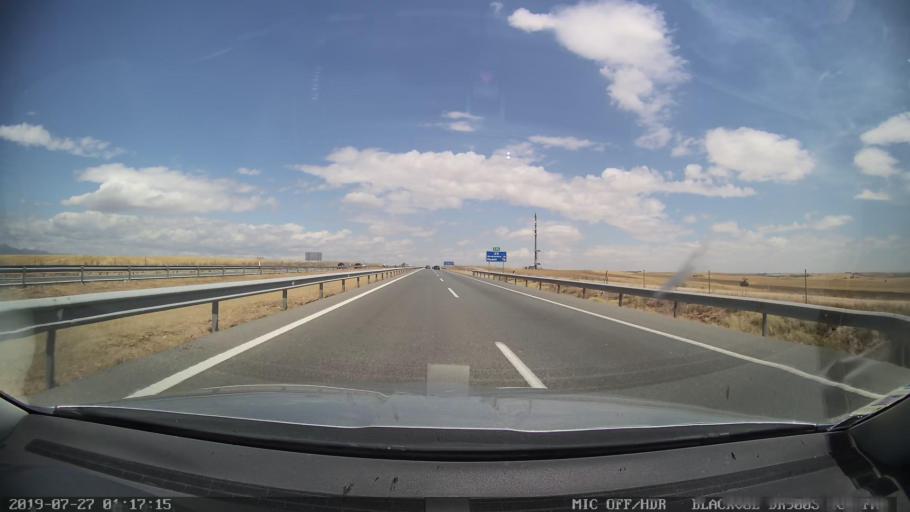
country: ES
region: Castille-La Mancha
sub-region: Province of Toledo
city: Maqueda
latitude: 40.0762
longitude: -4.3597
